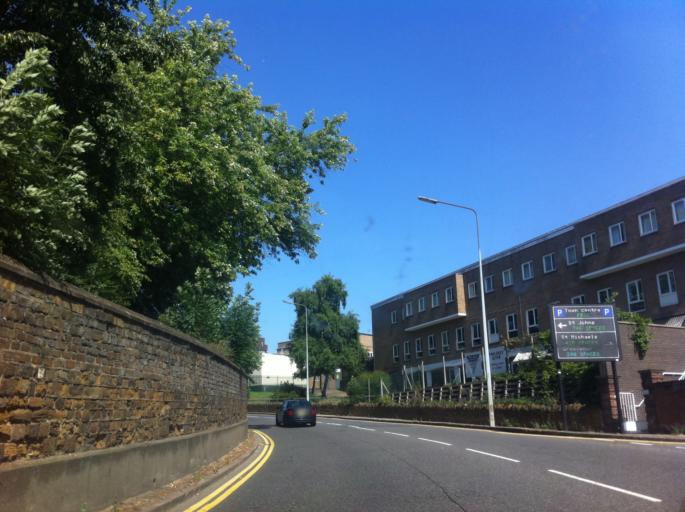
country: GB
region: England
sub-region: Northamptonshire
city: Northampton
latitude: 52.2330
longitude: -0.8833
